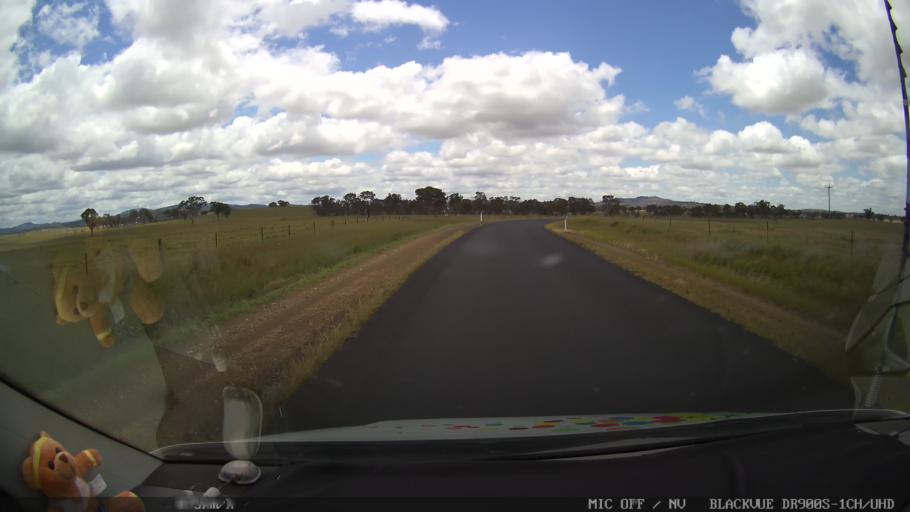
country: AU
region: New South Wales
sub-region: Glen Innes Severn
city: Glen Innes
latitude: -29.4372
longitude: 151.8317
